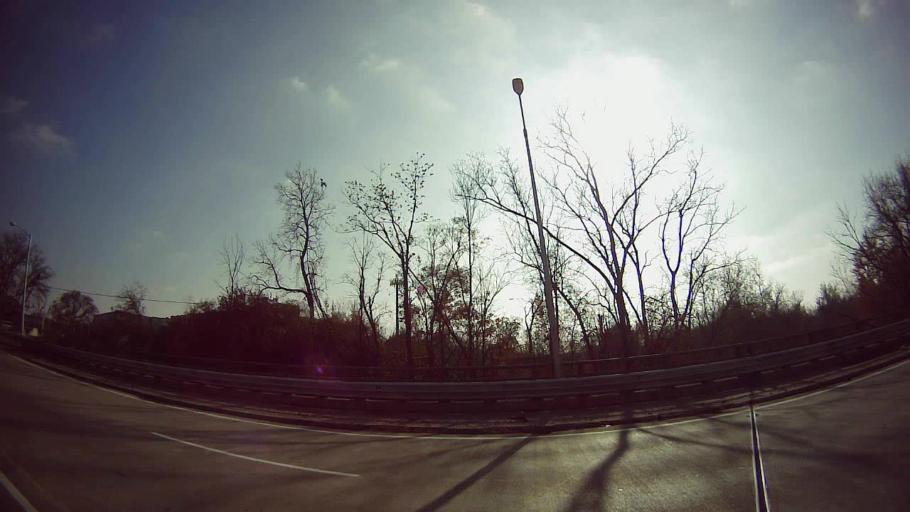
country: US
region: Michigan
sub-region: Wayne County
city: Dearborn Heights
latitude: 42.3274
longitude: -83.2425
